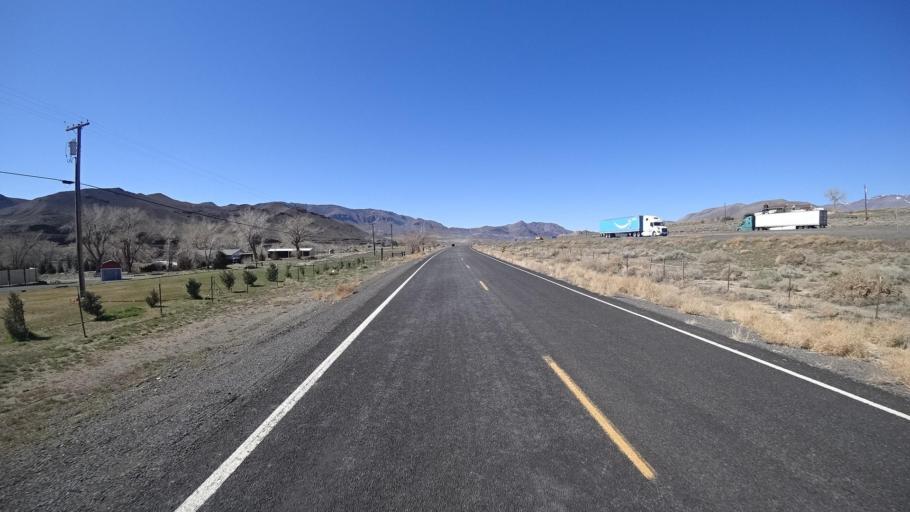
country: US
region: Nevada
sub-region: Lyon County
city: Fernley
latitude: 39.6072
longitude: -119.3227
